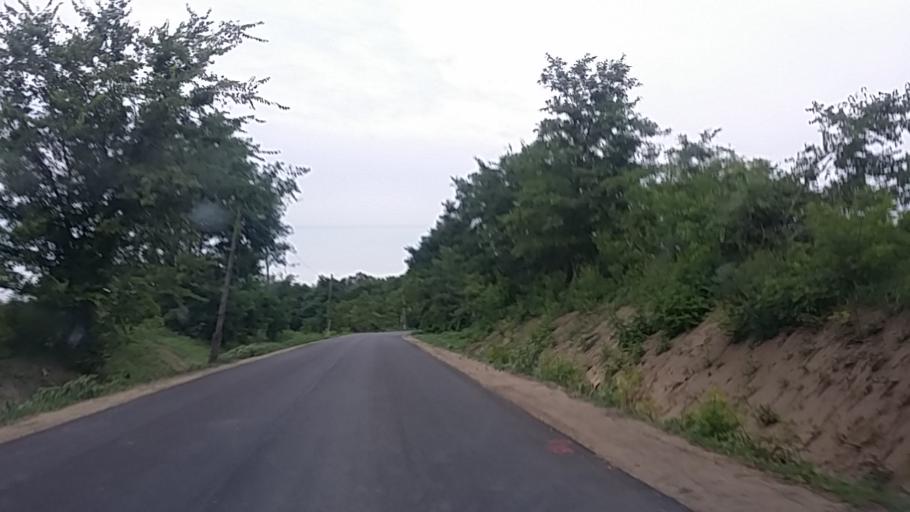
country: HU
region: Tolna
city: Tengelic
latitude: 46.5479
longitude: 18.6992
